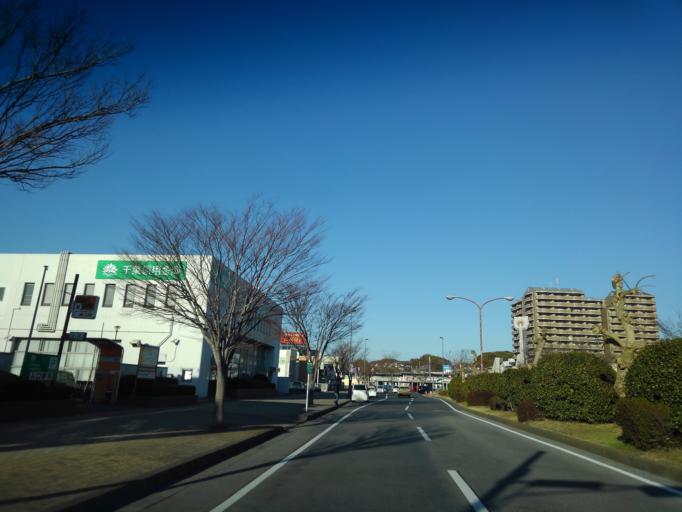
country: JP
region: Chiba
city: Kimitsu
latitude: 35.3324
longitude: 139.8938
